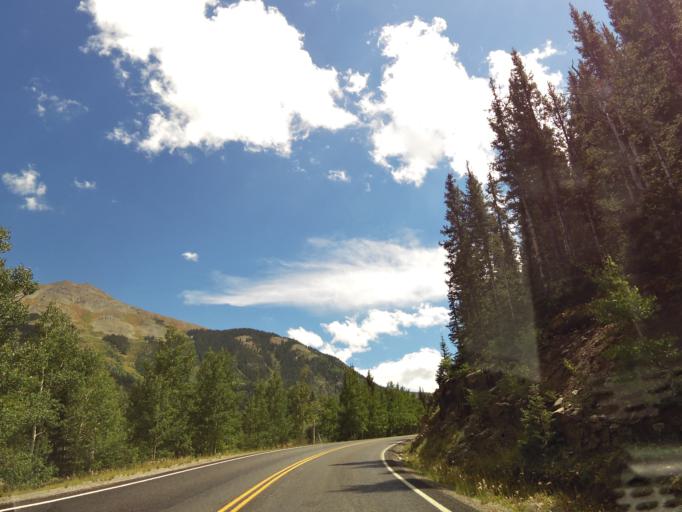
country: US
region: Colorado
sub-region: San Juan County
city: Silverton
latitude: 37.8001
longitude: -107.6754
